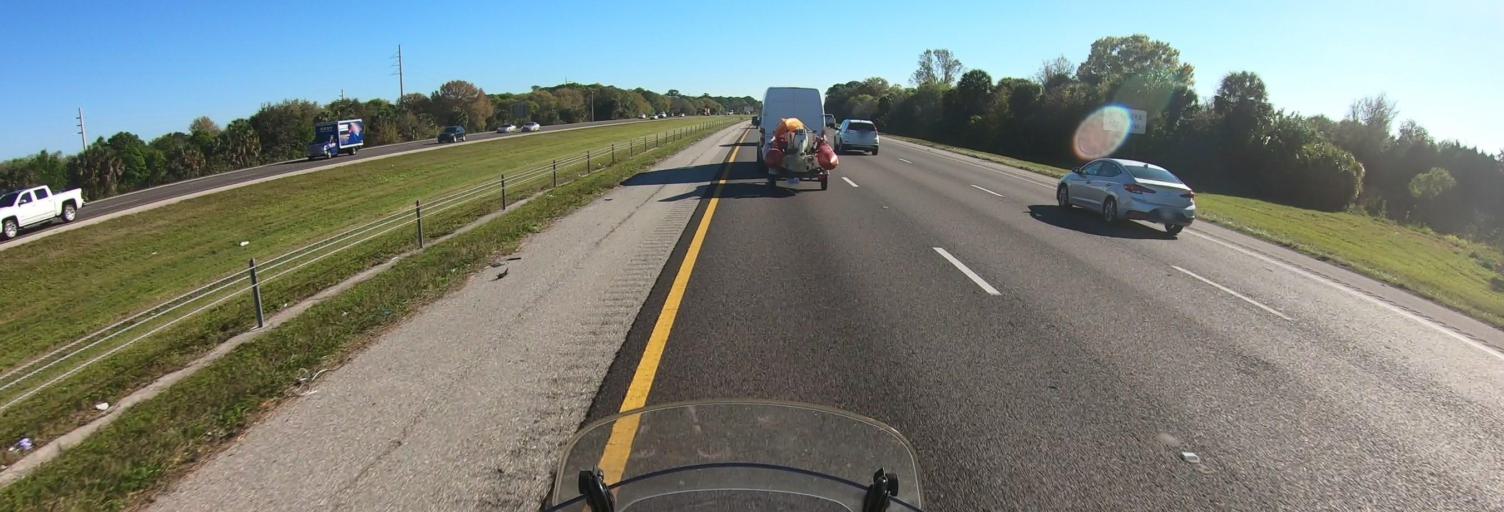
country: US
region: Florida
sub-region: Sarasota County
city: Lake Sarasota
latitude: 27.2515
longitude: -82.4511
